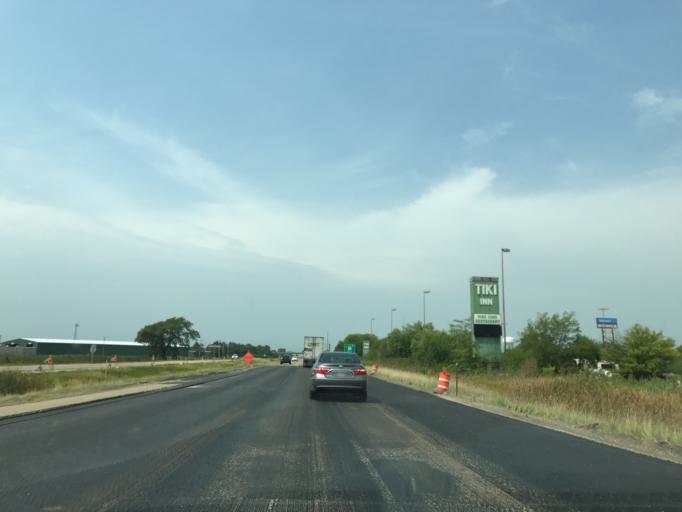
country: US
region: Illinois
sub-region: LaSalle County
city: Peru
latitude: 41.3656
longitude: -89.1167
